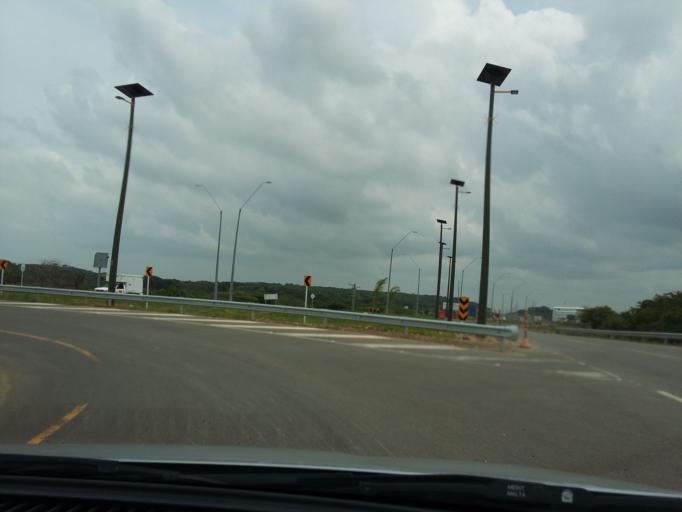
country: CO
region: Bolivar
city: Cartagena
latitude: 10.5009
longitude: -75.4753
